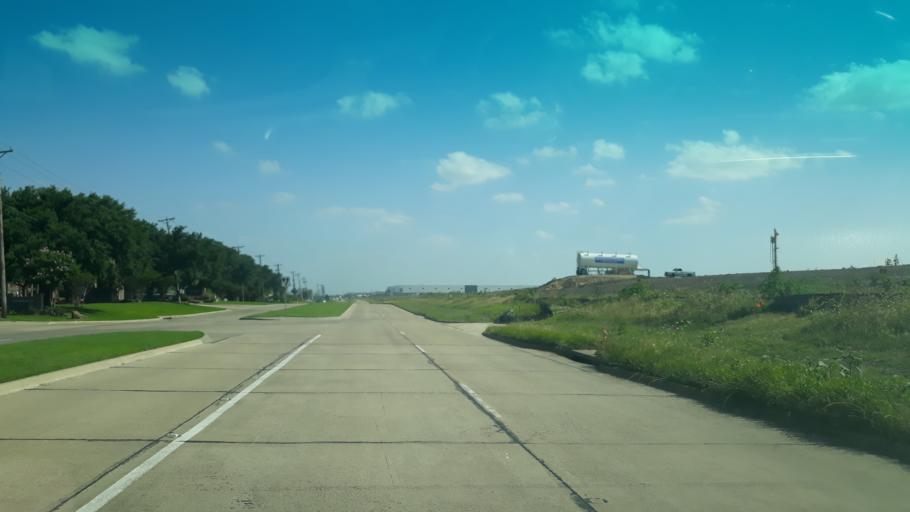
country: US
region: Texas
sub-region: Tarrant County
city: Euless
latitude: 32.8536
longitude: -97.0216
